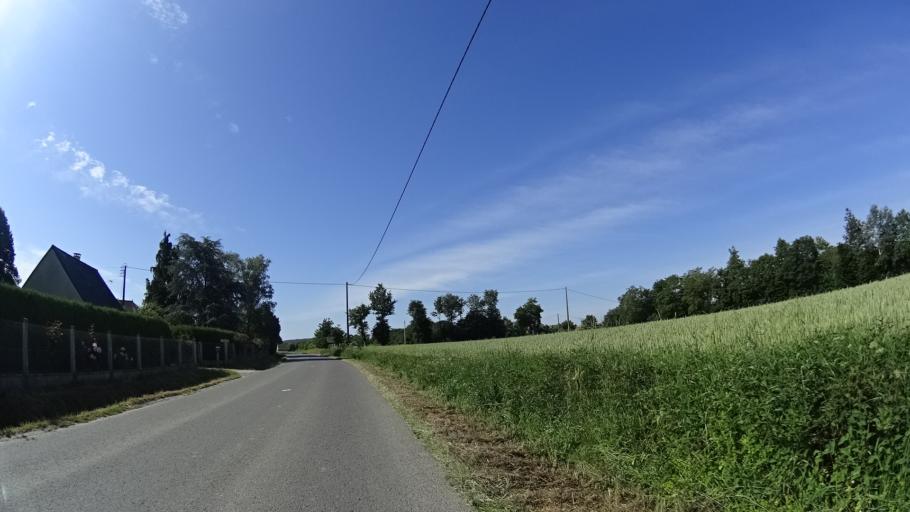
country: FR
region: Brittany
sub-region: Departement d'Ille-et-Vilaine
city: Guipry
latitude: 47.8050
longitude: -1.8492
